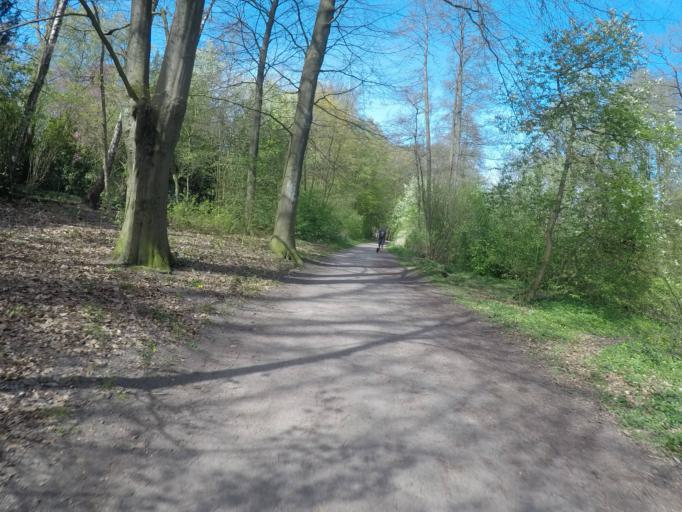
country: DE
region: Hamburg
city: Wellingsbuettel
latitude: 53.6492
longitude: 10.0815
